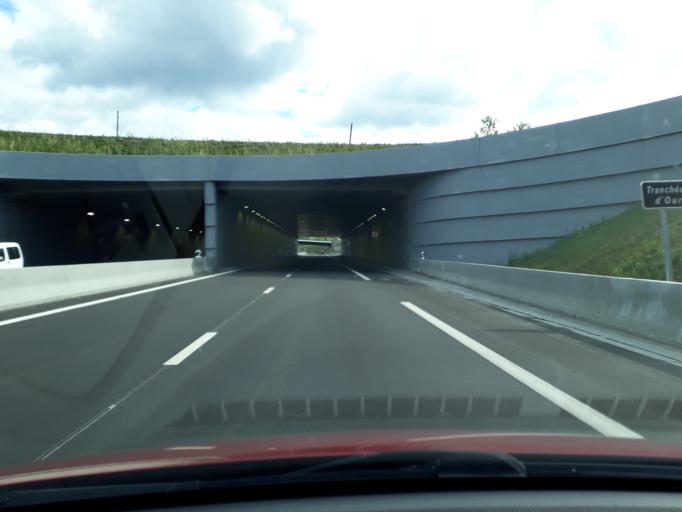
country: FR
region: Auvergne
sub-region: Departement de la Haute-Loire
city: Le Puy-en-Velay
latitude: 45.0371
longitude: 3.9073
